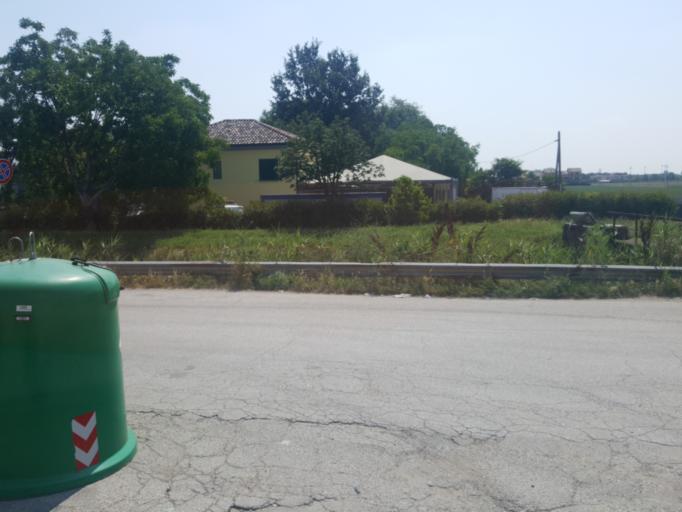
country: IT
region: Emilia-Romagna
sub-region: Provincia di Ravenna
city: Massa Lombarda
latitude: 44.4555
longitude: 11.7949
